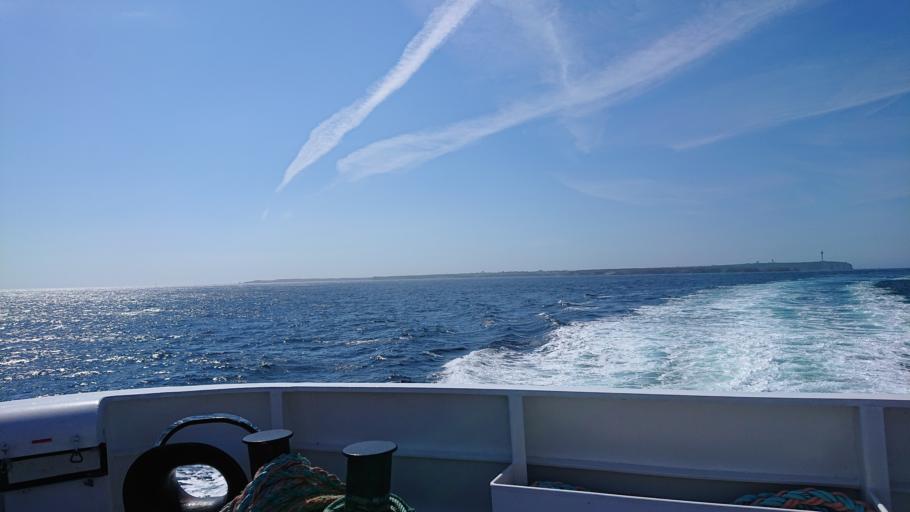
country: FR
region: Brittany
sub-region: Departement du Finistere
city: Porspoder
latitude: 48.4480
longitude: -5.0021
